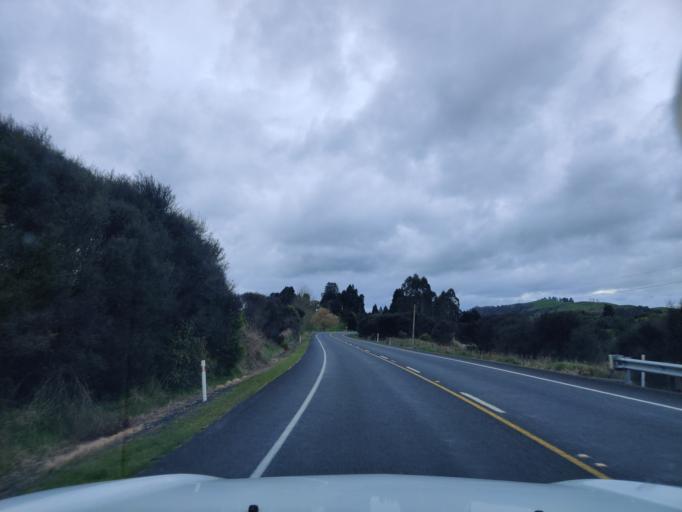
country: NZ
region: Waikato
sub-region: Otorohanga District
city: Otorohanga
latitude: -38.5026
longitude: 175.2038
